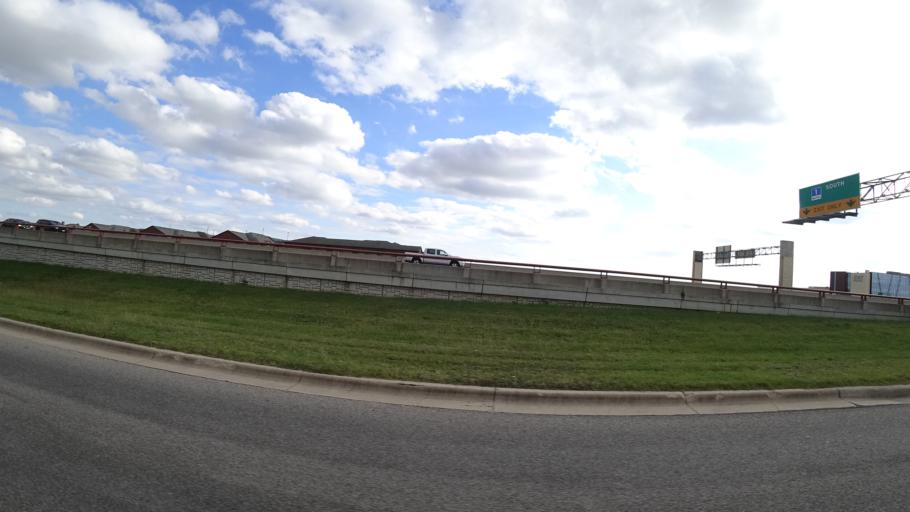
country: US
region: Texas
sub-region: Williamson County
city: Round Rock
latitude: 30.4792
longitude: -97.6881
